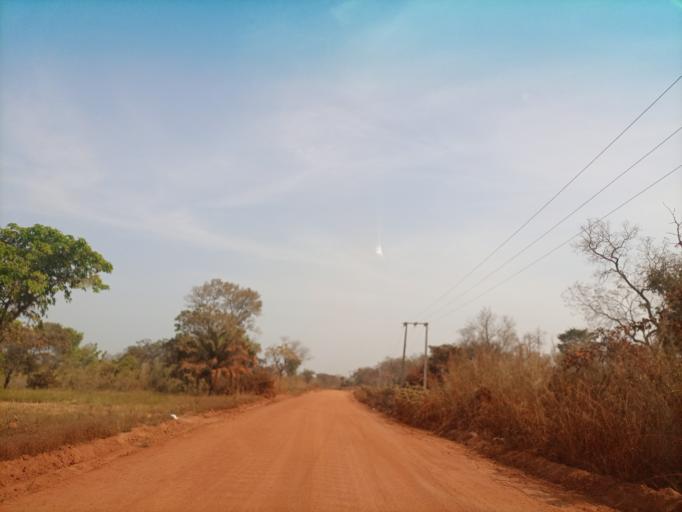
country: NG
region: Enugu
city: Eha Amufu
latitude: 6.6705
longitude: 7.7387
